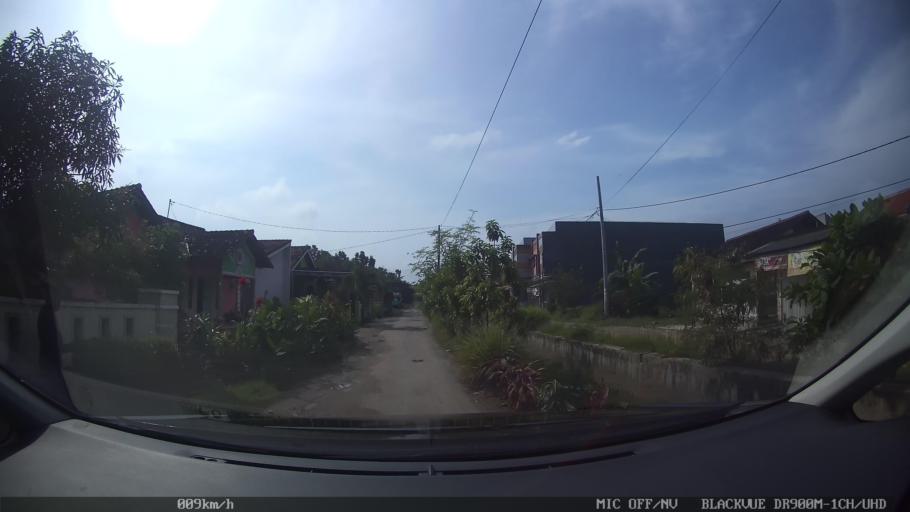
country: ID
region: Lampung
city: Kedaton
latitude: -5.3784
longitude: 105.2997
